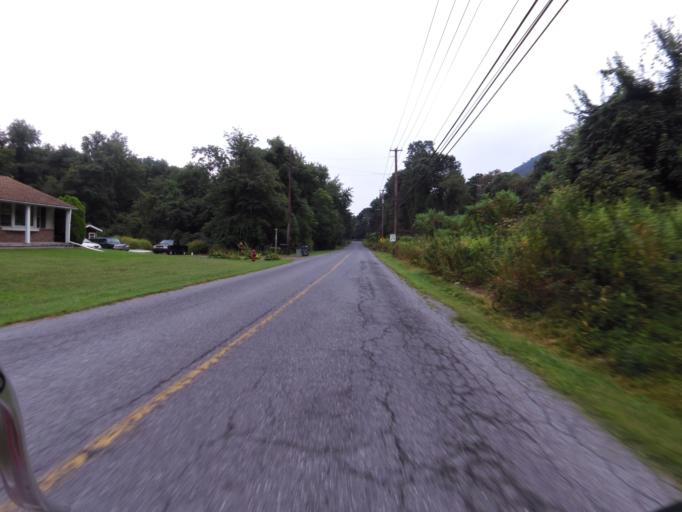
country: US
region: Pennsylvania
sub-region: Perry County
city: Marysville
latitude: 40.3339
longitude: -76.9211
